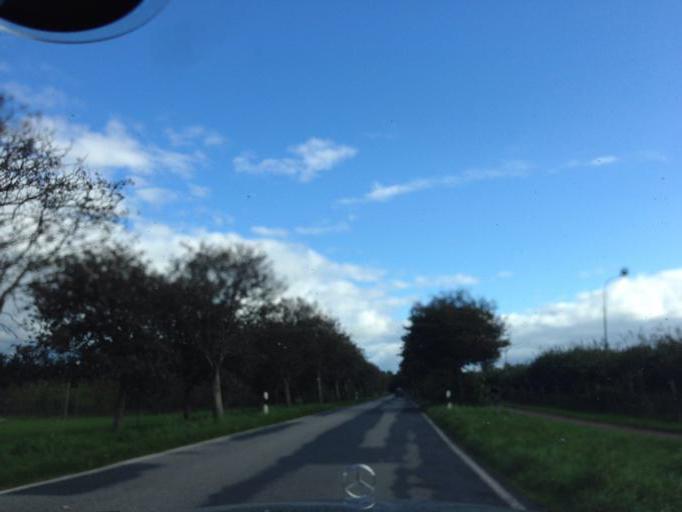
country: DE
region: Schleswig-Holstein
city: Niebull
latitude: 54.7774
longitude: 8.8408
